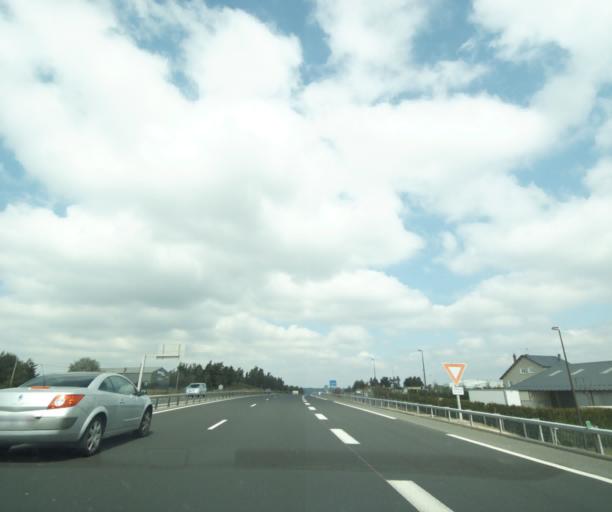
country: FR
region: Languedoc-Roussillon
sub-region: Departement de la Lozere
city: Aumont-Aubrac
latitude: 44.7352
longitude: 3.2897
